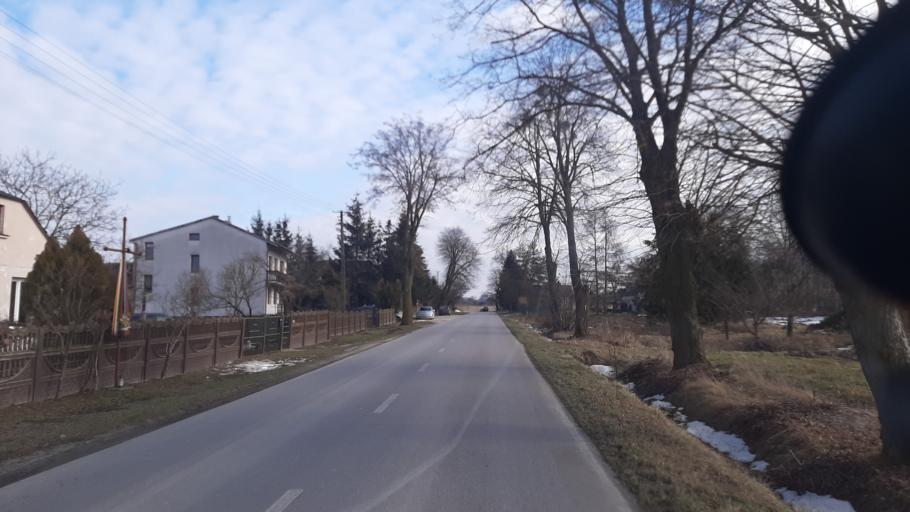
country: PL
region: Lublin Voivodeship
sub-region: Powiat lubartowski
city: Uscimow Stary
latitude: 51.4791
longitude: 22.9190
